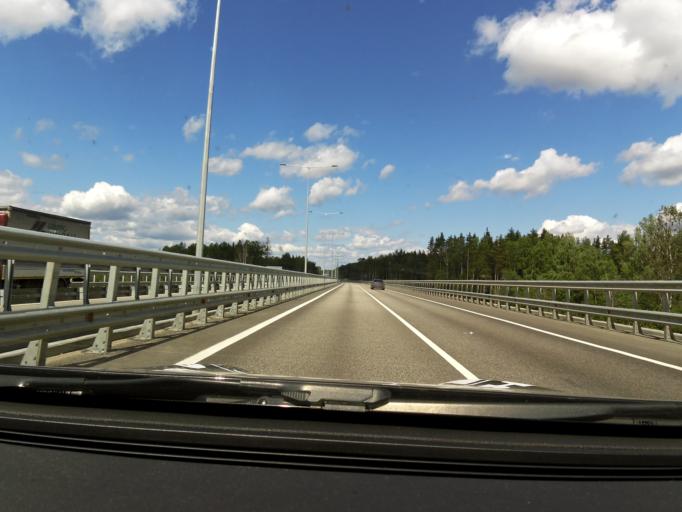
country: RU
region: Tverskaya
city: Vydropuzhsk
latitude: 57.3391
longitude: 34.7268
